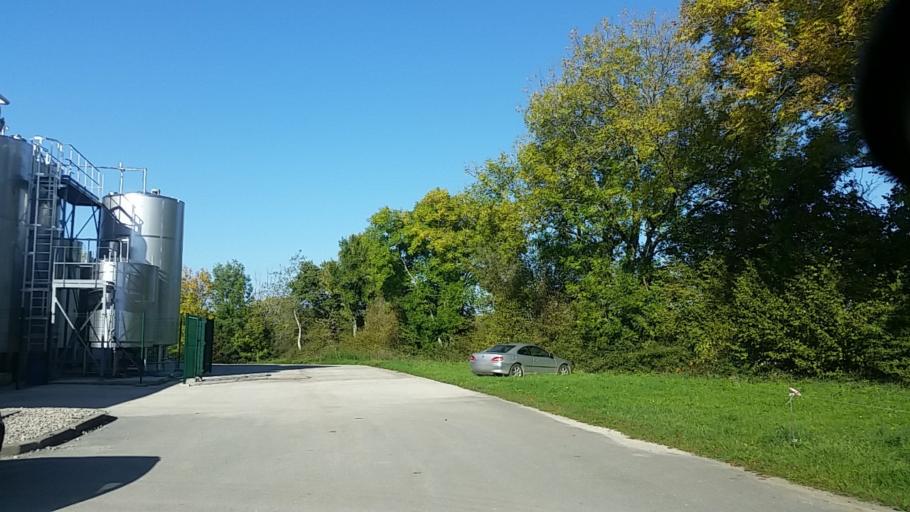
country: FR
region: Franche-Comte
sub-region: Departement du Doubs
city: Ornans
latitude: 47.0436
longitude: 6.0687
